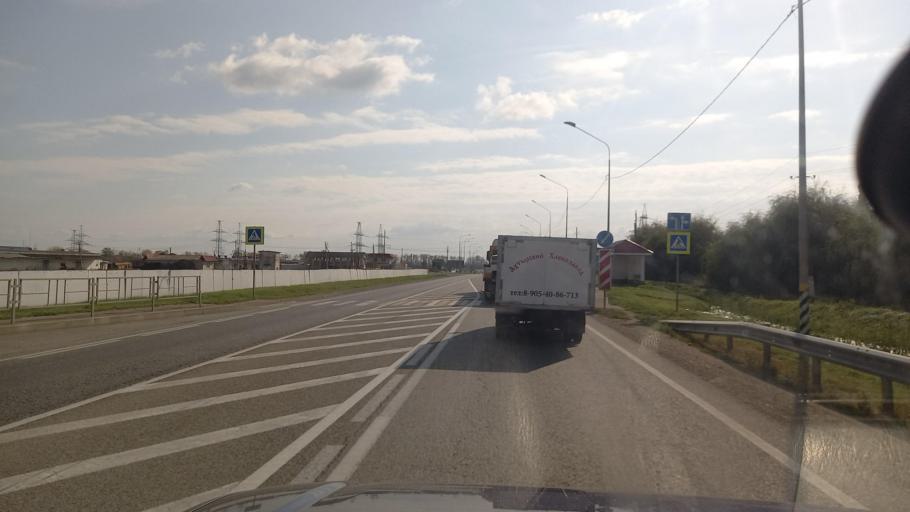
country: RU
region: Krasnodarskiy
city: Novoukrainskiy
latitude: 44.9069
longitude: 38.0261
